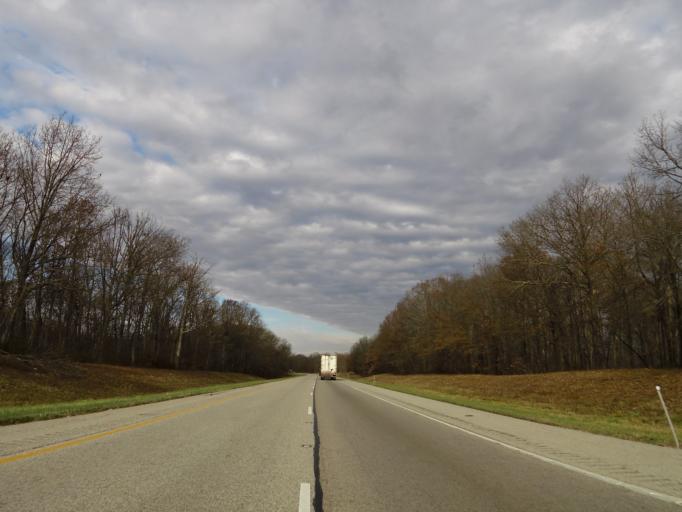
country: US
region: Illinois
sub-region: Washington County
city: Nashville
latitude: 38.4035
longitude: -89.4034
